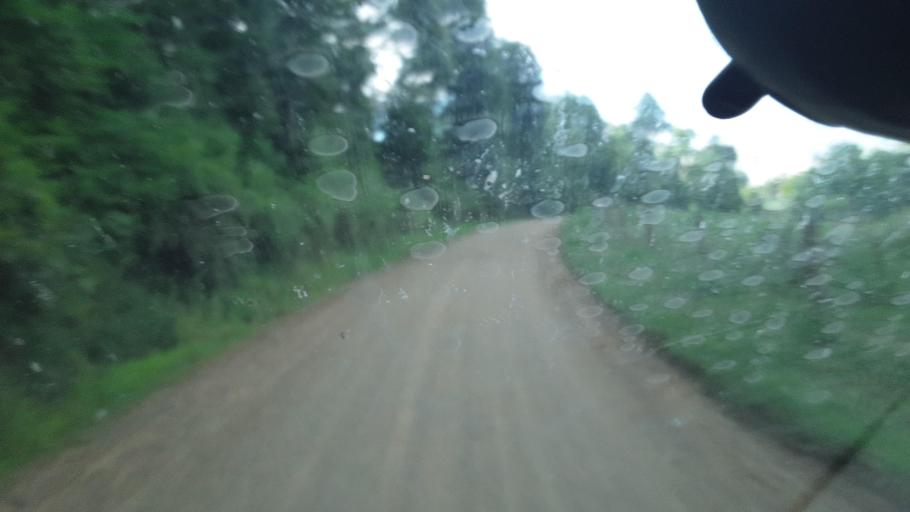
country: US
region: Ohio
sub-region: Holmes County
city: Millersburg
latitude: 40.4309
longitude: -81.8487
